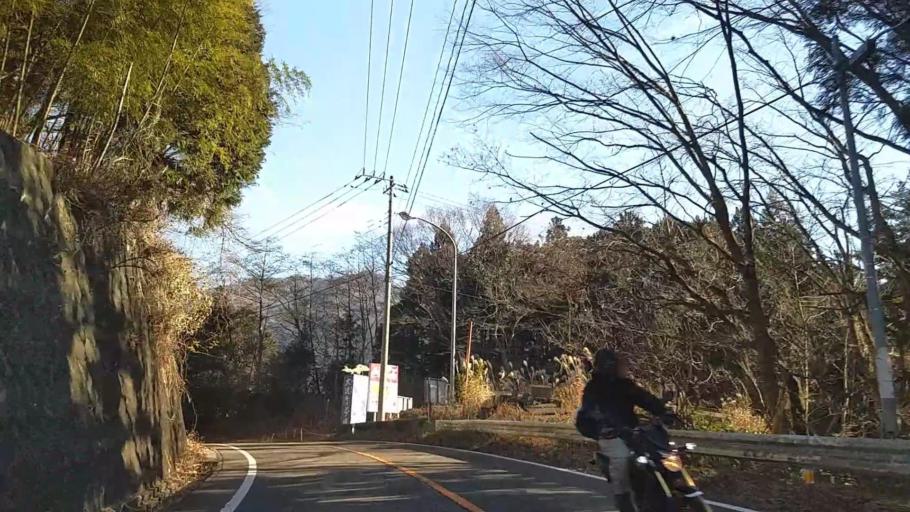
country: JP
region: Yamanashi
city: Uenohara
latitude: 35.5288
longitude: 139.0970
